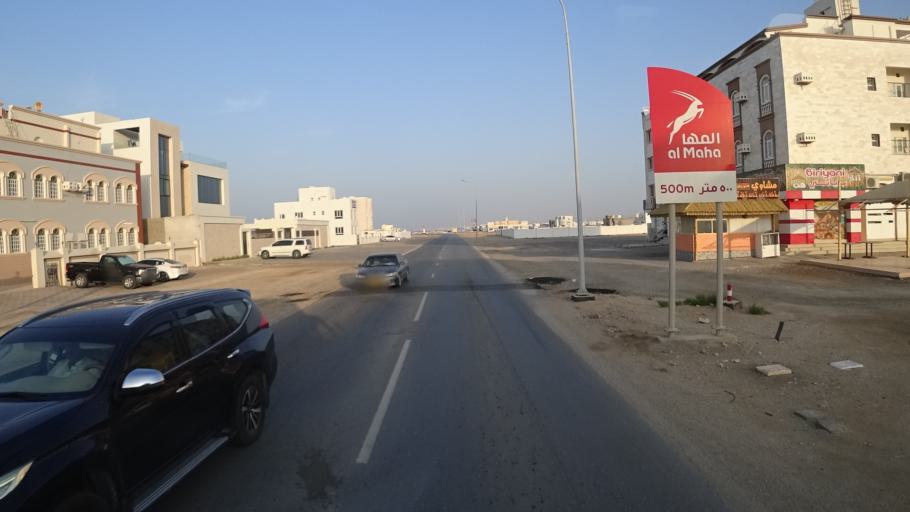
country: OM
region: Ash Sharqiyah
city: Sur
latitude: 22.6058
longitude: 59.4770
